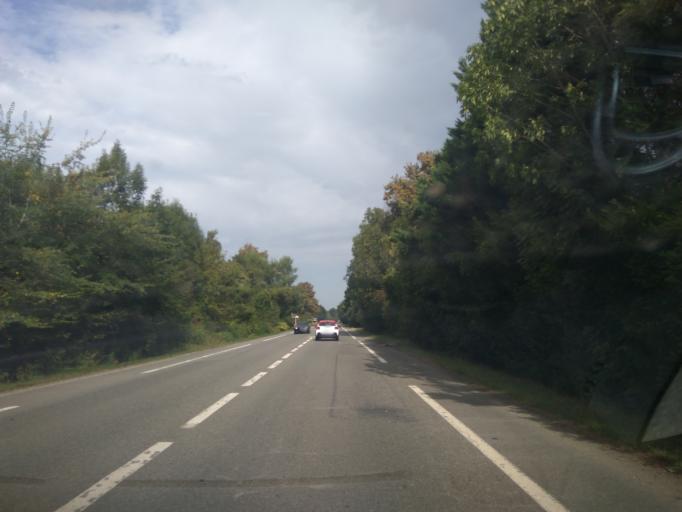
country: FR
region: Aquitaine
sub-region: Departement des Pyrenees-Atlantiques
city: Artiguelouve
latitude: 43.3195
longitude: -0.4644
